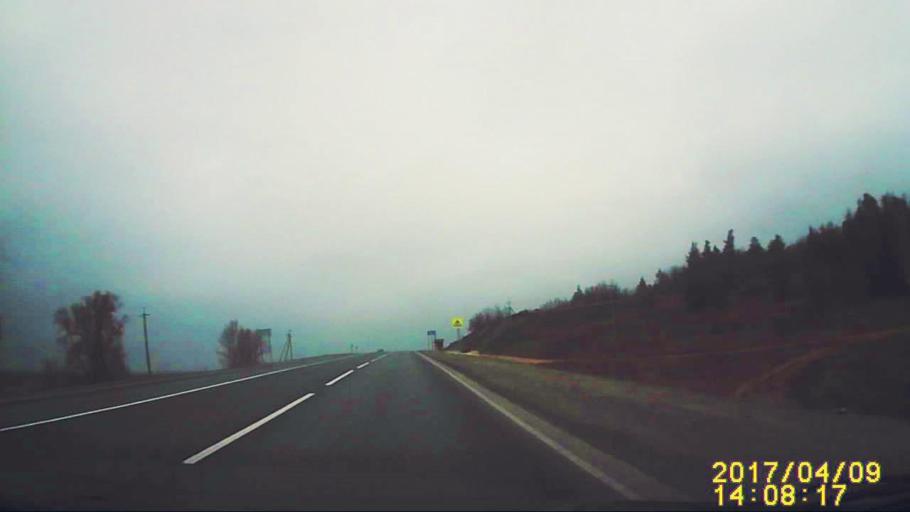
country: RU
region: Ulyanovsk
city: Silikatnyy
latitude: 54.0190
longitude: 48.2158
